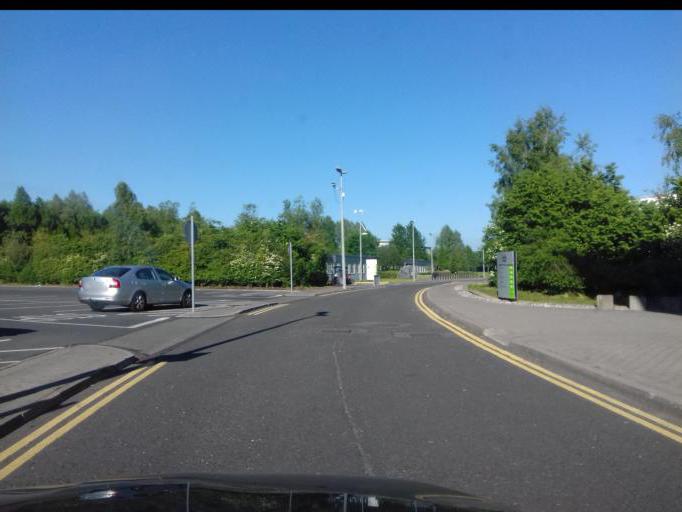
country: IE
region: Leinster
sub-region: Fingal County
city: Blanchardstown
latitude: 53.4060
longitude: -6.3783
